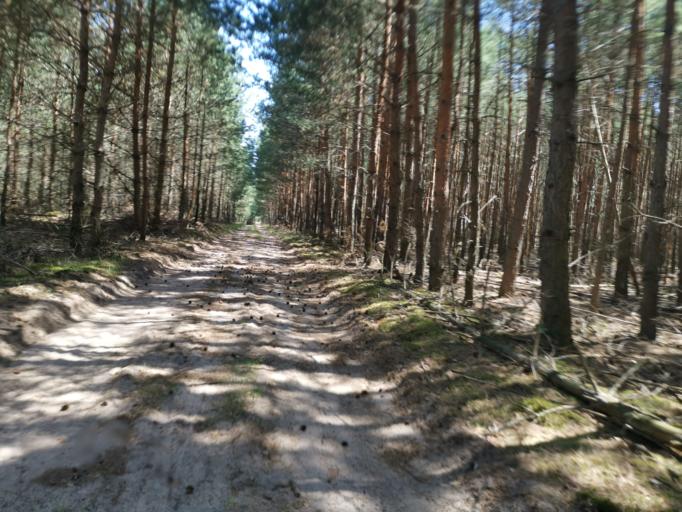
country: CZ
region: South Moravian
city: Vracov
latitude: 48.9502
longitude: 17.2295
